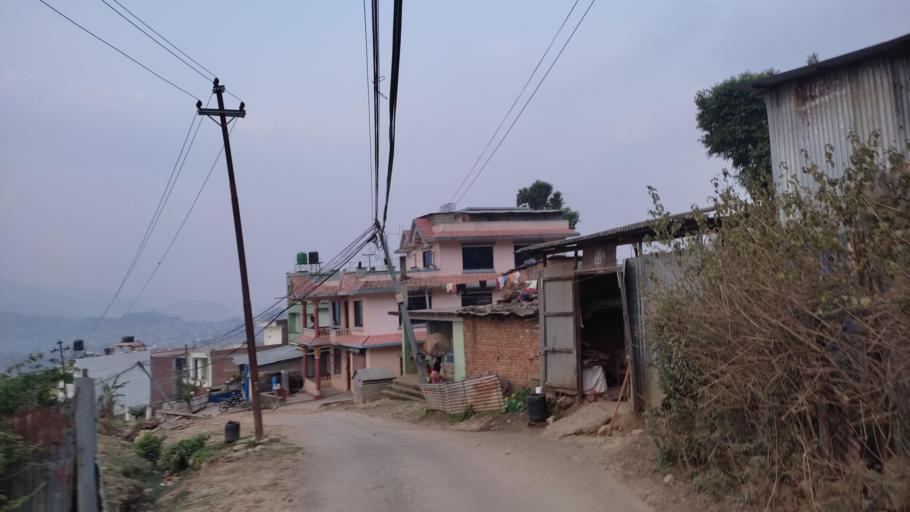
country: NP
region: Central Region
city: Kirtipur
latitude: 27.6717
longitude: 85.2443
